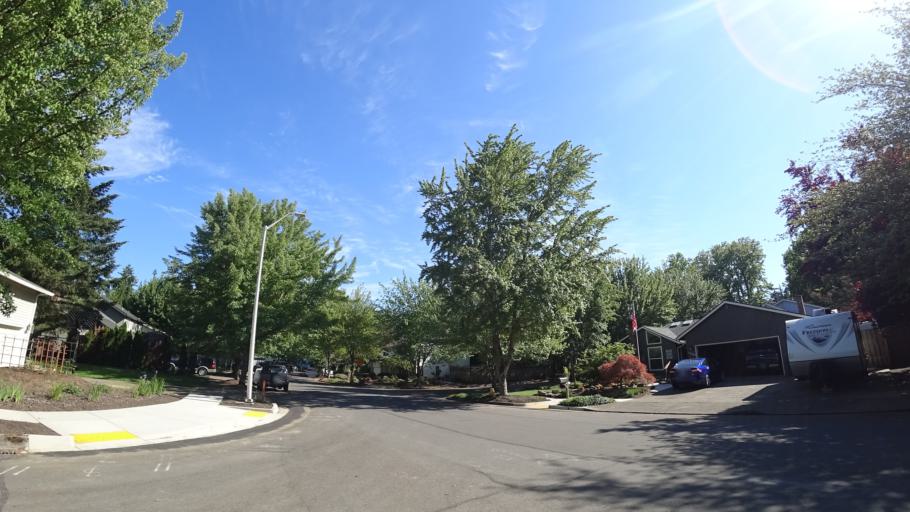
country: US
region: Oregon
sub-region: Washington County
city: Beaverton
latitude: 45.4532
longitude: -122.8074
